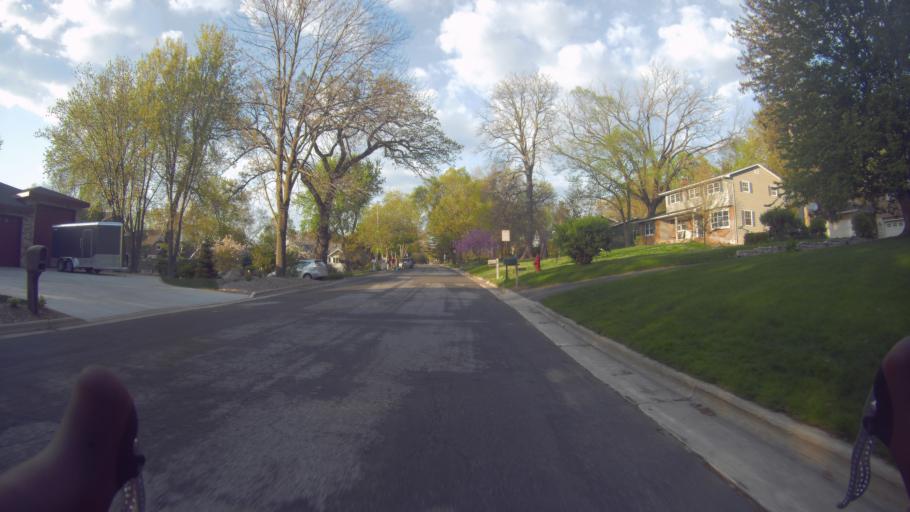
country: US
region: Wisconsin
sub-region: Dane County
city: Monona
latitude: 43.0727
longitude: -89.3302
